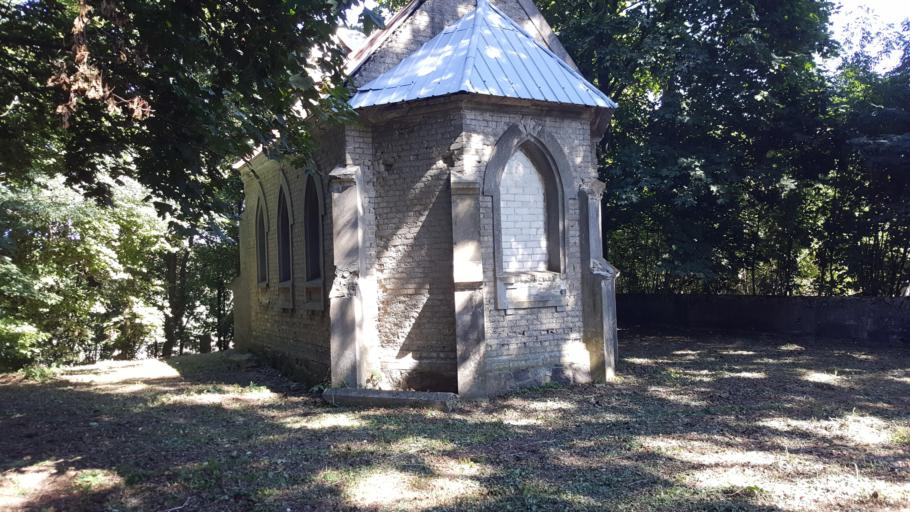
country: PL
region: Lublin Voivodeship
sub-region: Powiat bialski
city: Terespol
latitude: 52.2179
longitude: 23.5101
